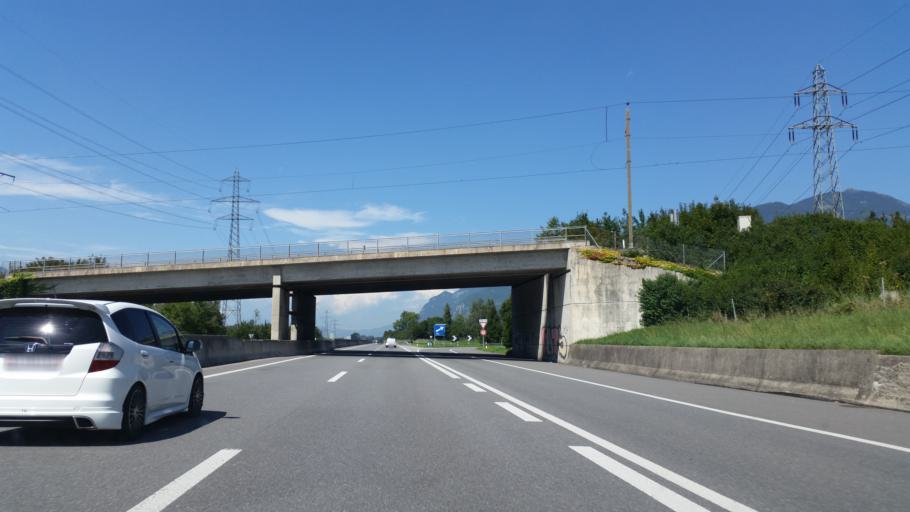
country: CH
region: Valais
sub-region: Monthey District
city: Collombey
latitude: 46.2773
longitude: 6.9697
